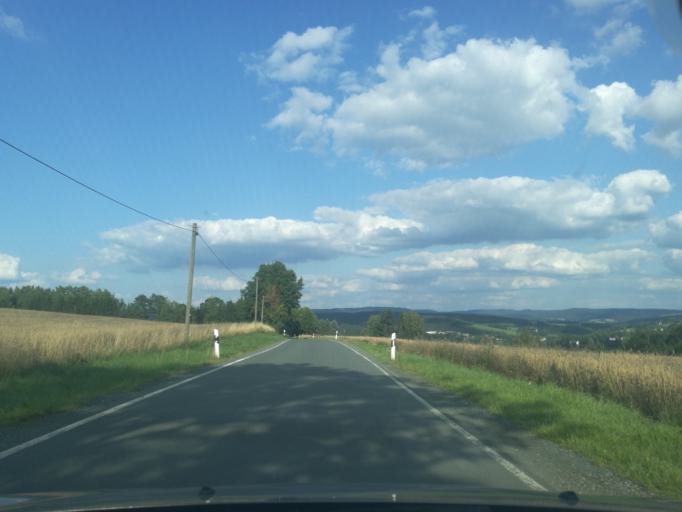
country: DE
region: Saxony
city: Adorf
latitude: 50.3175
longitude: 12.2402
